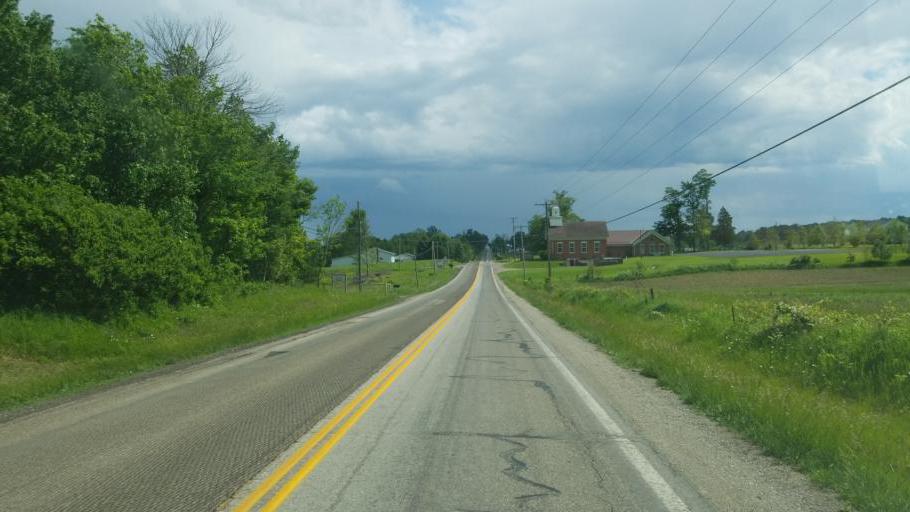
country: US
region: Ohio
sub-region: Richland County
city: Lexington
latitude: 40.6031
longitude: -82.6624
